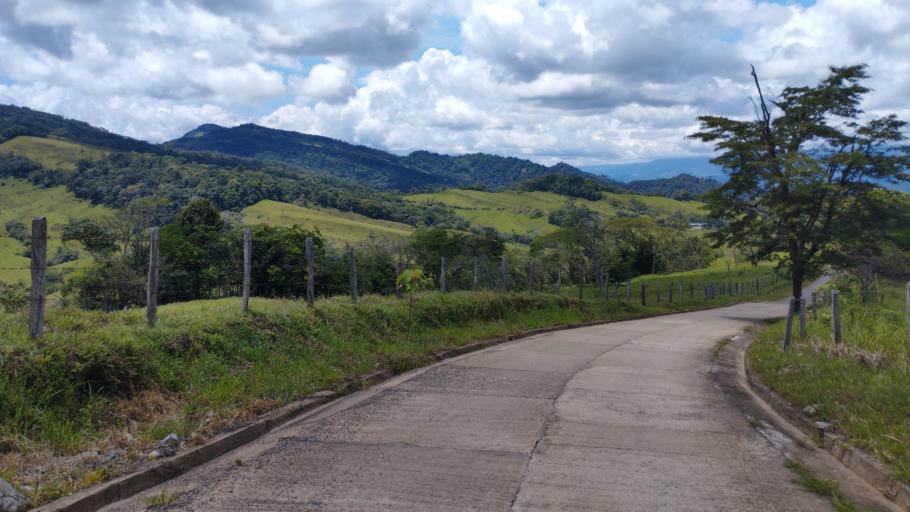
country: CO
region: Boyaca
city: San Luis de Gaceno
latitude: 4.7763
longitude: -73.1268
